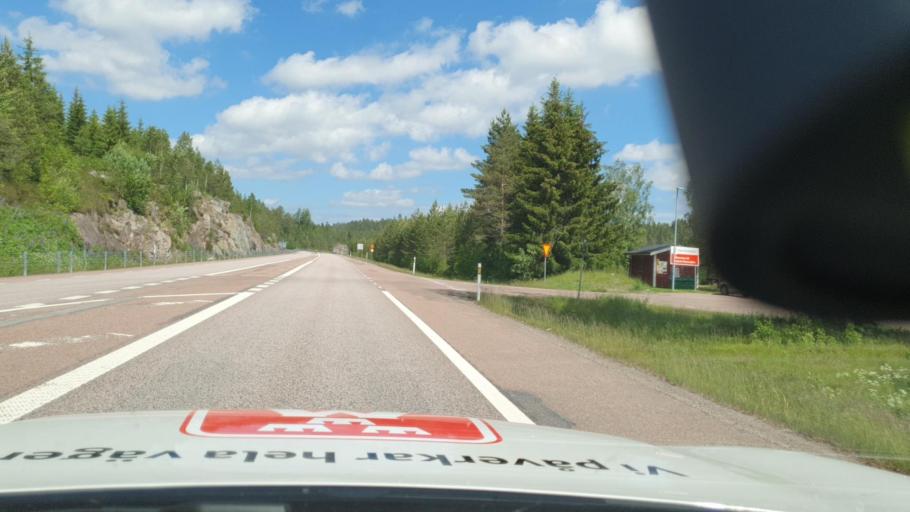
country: SE
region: Vaermland
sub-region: Filipstads Kommun
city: Filipstad
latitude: 59.6907
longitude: 14.0834
